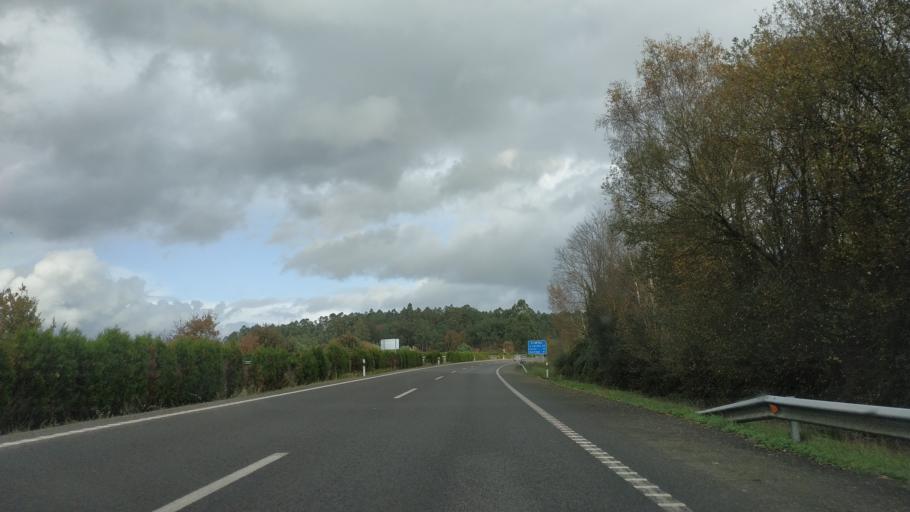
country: ES
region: Galicia
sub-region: Provincia da Coruna
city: Abegondo
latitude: 43.2502
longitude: -8.2821
